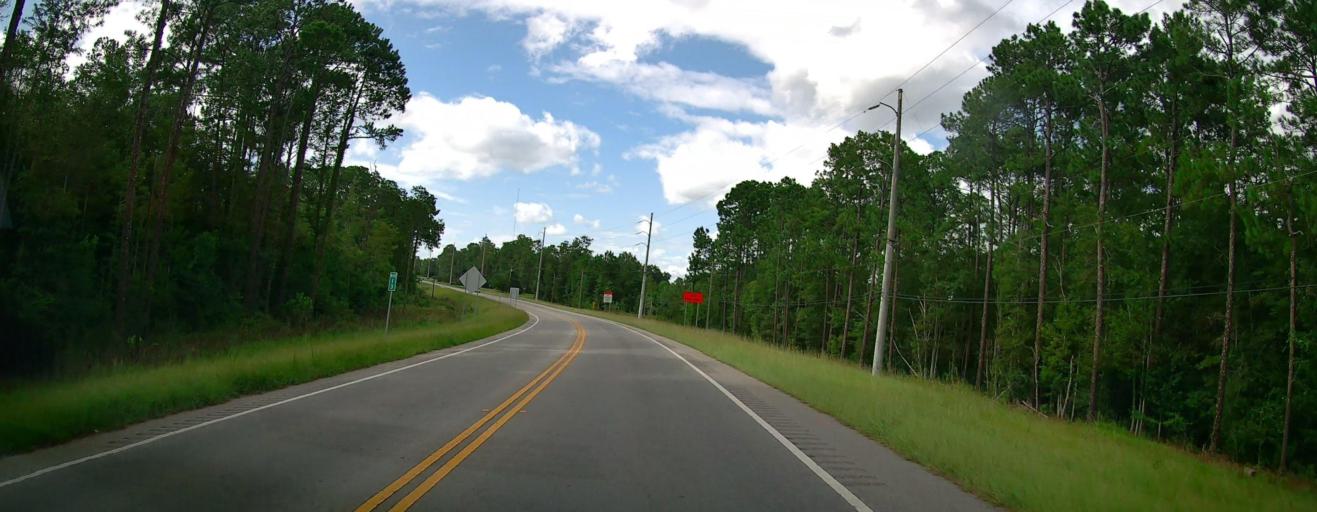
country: US
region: Georgia
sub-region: Coffee County
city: Douglas
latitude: 31.5165
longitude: -82.8700
